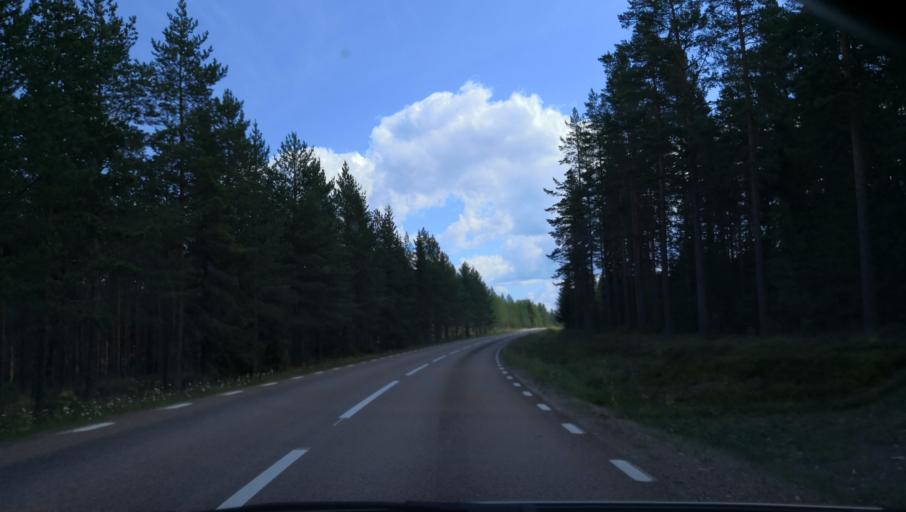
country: SE
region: Dalarna
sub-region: Rattviks Kommun
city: Vikarbyn
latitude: 61.1638
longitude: 15.0283
